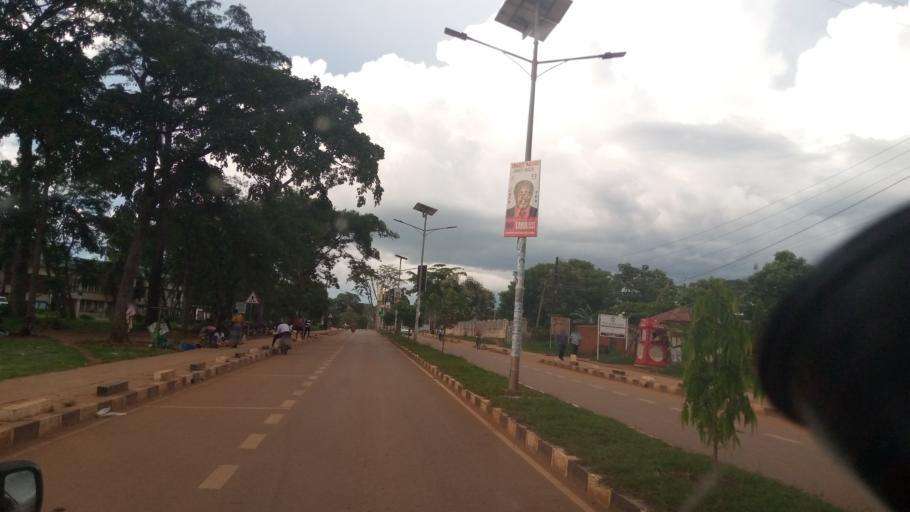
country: UG
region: Northern Region
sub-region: Lira District
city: Lira
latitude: 2.2470
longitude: 32.8997
